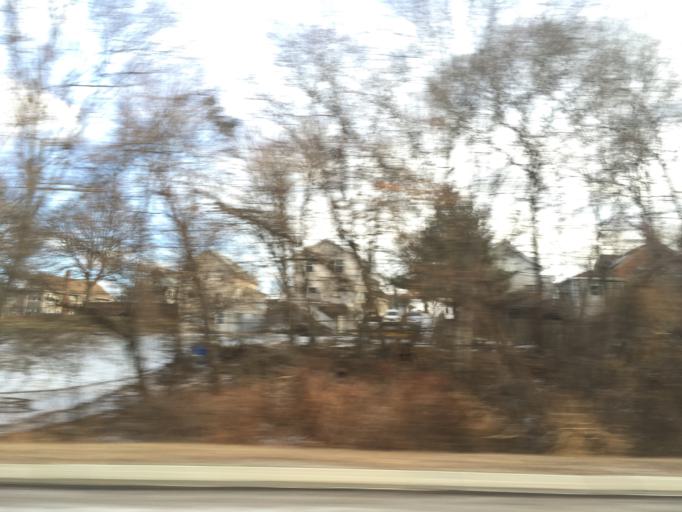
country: US
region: Rhode Island
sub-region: Providence County
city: Cranston
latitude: 41.7844
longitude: -71.4321
